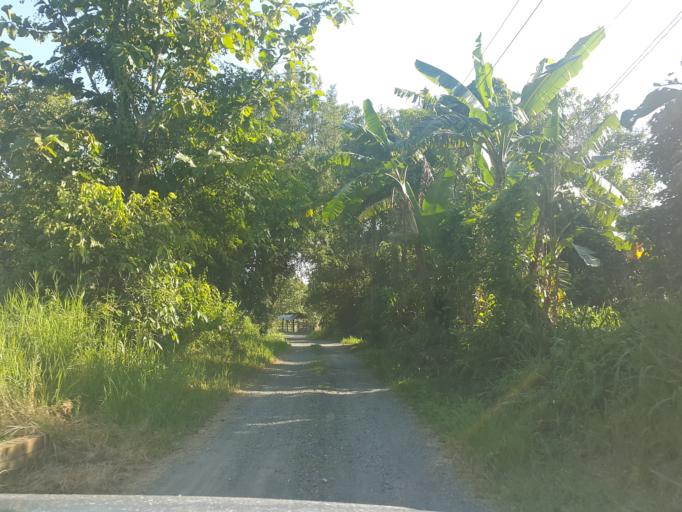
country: TH
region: Chiang Mai
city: Mae On
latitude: 18.7091
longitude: 99.2019
